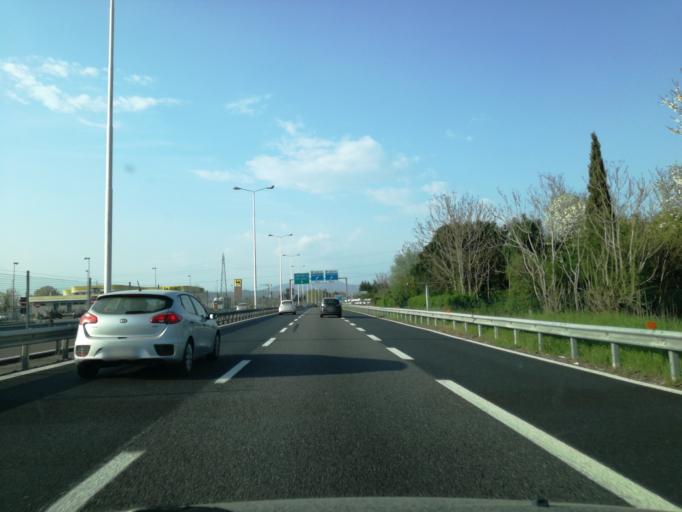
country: IT
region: Lombardy
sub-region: Provincia di Monza e Brianza
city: Velasca
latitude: 45.6346
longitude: 9.3635
